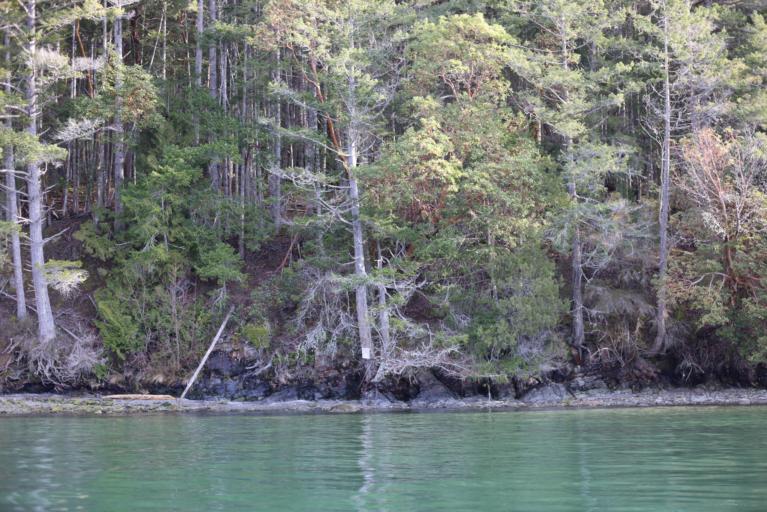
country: CA
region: British Columbia
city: Duncan
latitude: 48.7604
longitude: -123.5918
